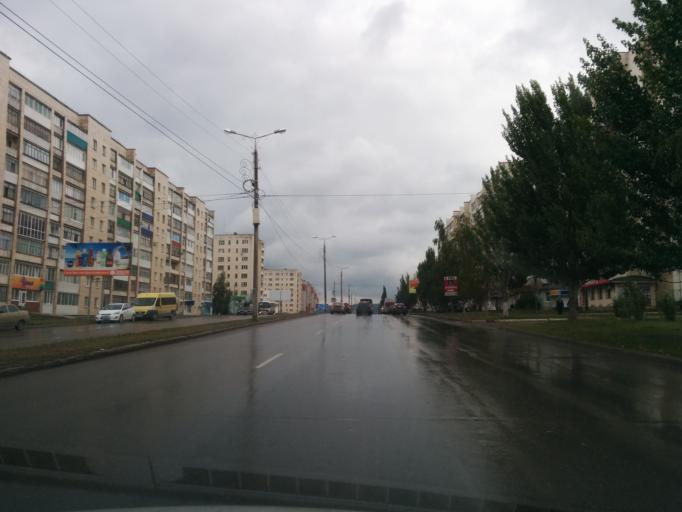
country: RU
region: Bashkortostan
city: Oktyabr'skiy
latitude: 54.4821
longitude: 53.5139
